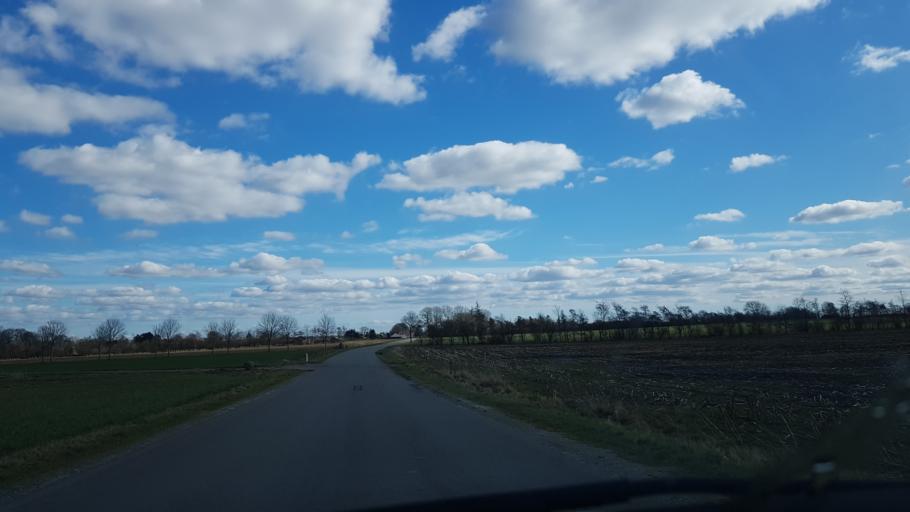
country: DK
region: South Denmark
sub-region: Vejen Kommune
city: Rodding
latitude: 55.3942
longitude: 9.0272
